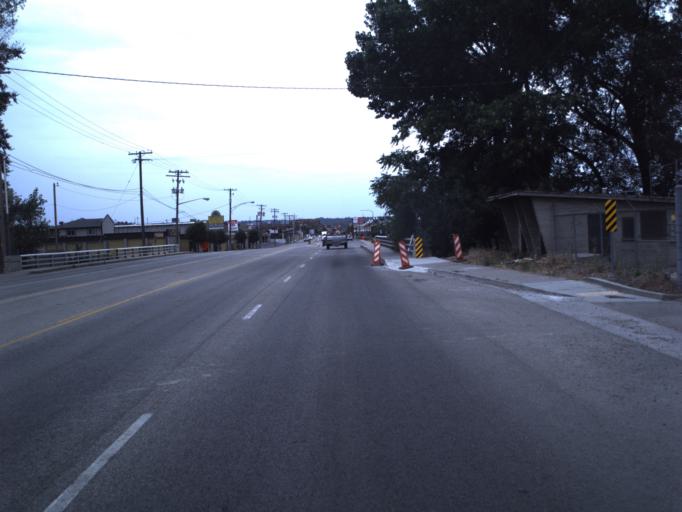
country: US
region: Utah
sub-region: Weber County
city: Ogden
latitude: 41.2349
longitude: -111.9786
